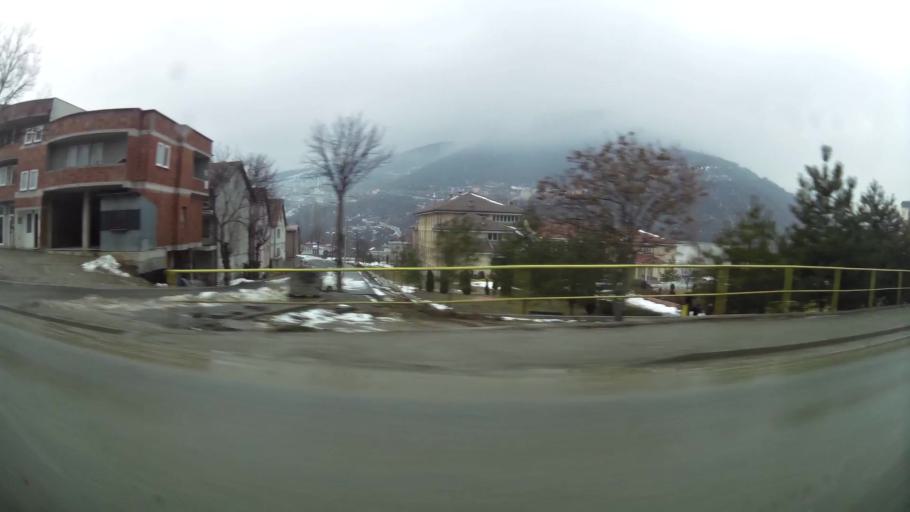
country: XK
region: Ferizaj
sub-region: Hani i Elezit
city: Hani i Elezit
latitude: 42.1537
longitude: 21.2967
